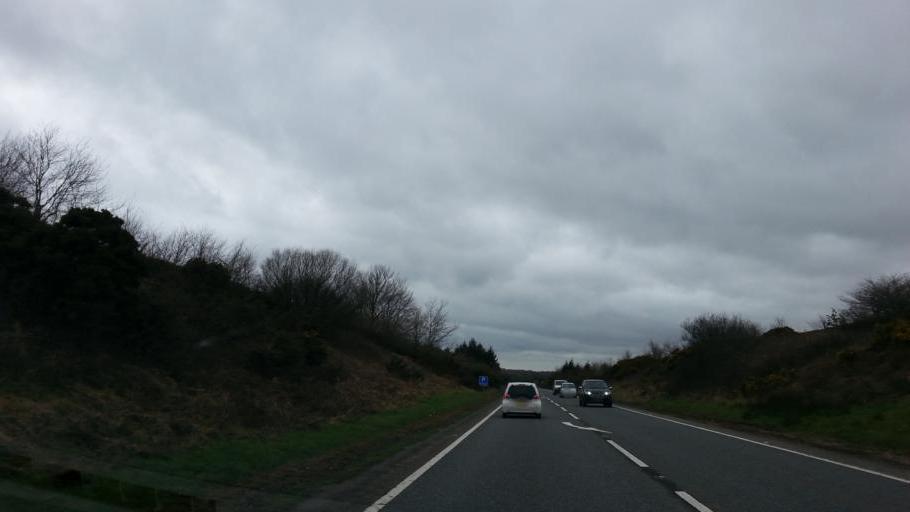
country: GB
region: England
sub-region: Devon
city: Tiverton
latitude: 50.9497
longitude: -3.6013
